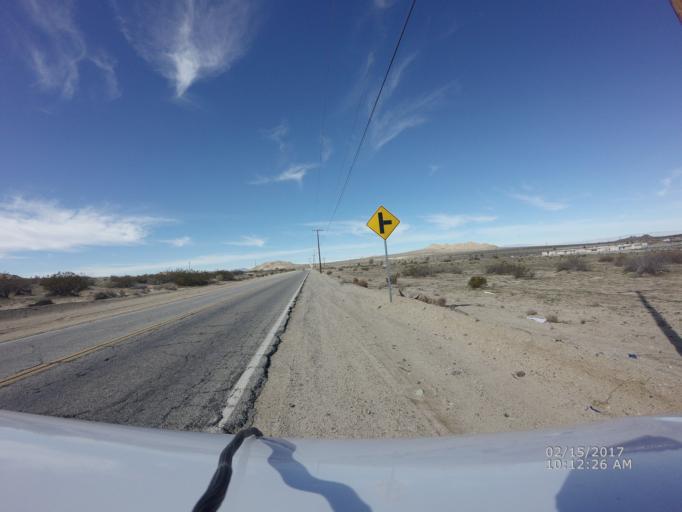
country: US
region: California
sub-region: Los Angeles County
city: Lake Los Angeles
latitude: 34.6165
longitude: -117.8598
